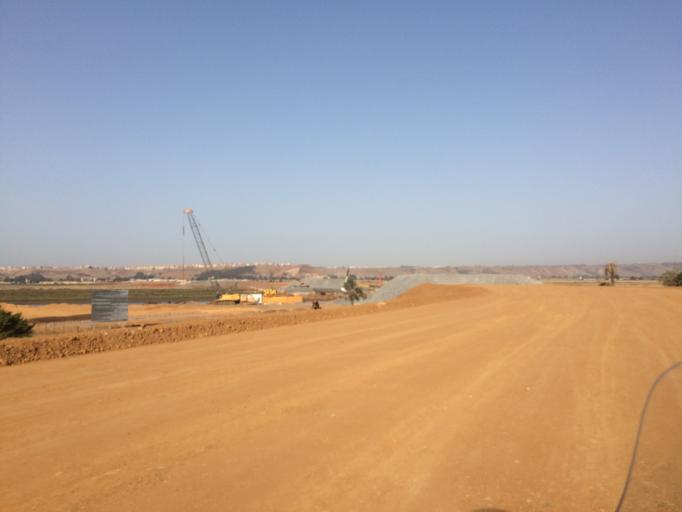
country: MA
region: Rabat-Sale-Zemmour-Zaer
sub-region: Rabat
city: Rabat
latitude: 34.0056
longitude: -6.8143
